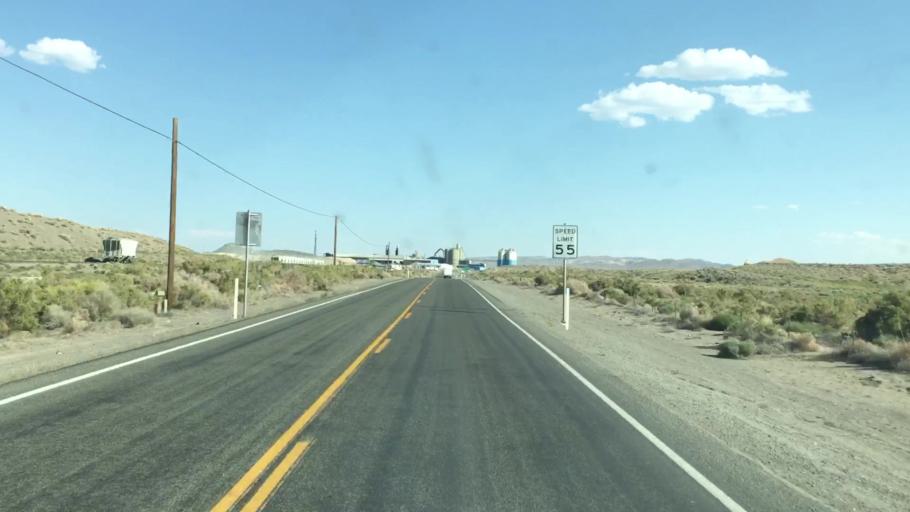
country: US
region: Nevada
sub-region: Lyon County
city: Fernley
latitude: 39.6286
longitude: -119.2749
